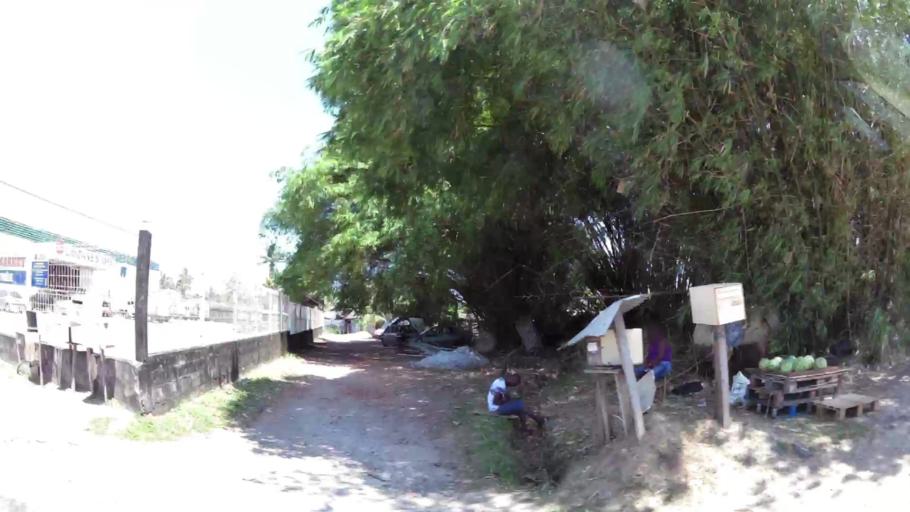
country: GF
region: Guyane
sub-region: Guyane
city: Cayenne
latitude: 4.9061
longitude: -52.3254
